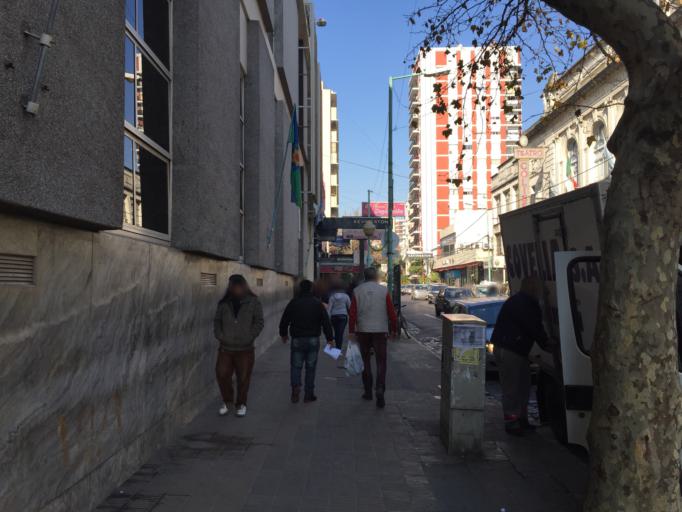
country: AR
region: Buenos Aires
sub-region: Partido de Lomas de Zamora
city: Lomas de Zamora
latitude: -34.7610
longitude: -58.3997
